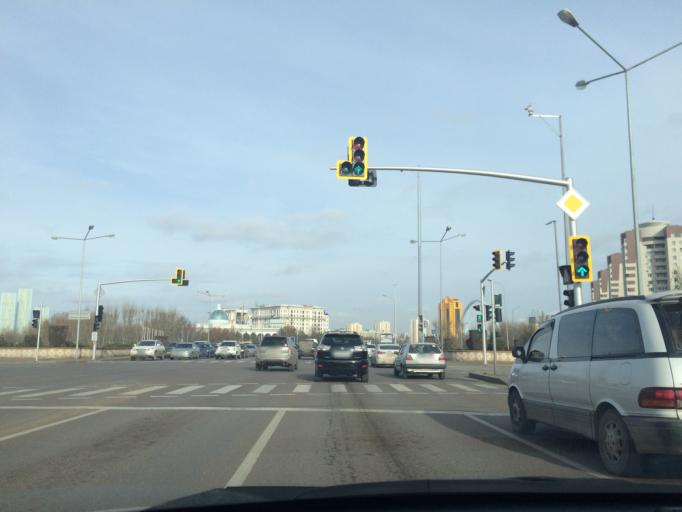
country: KZ
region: Astana Qalasy
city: Astana
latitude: 51.1469
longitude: 71.4224
